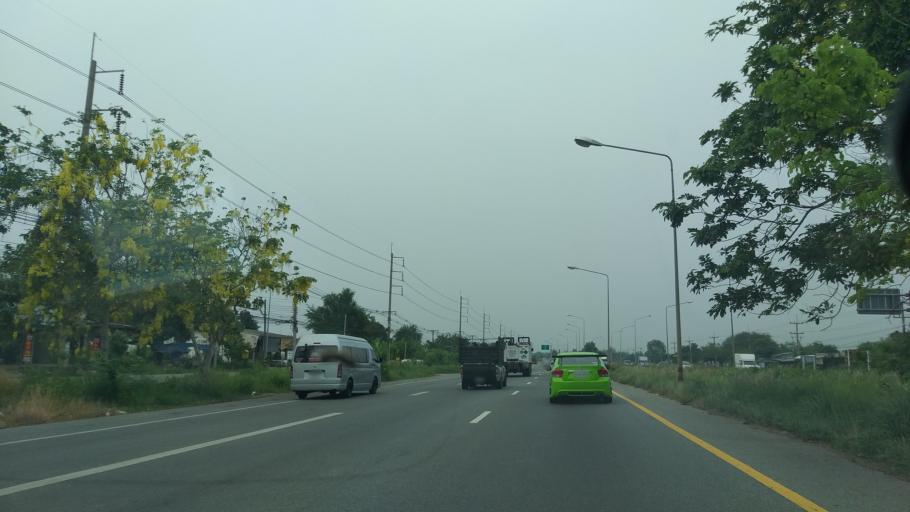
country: TH
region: Chon Buri
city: Ko Chan
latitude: 13.3915
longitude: 101.2799
